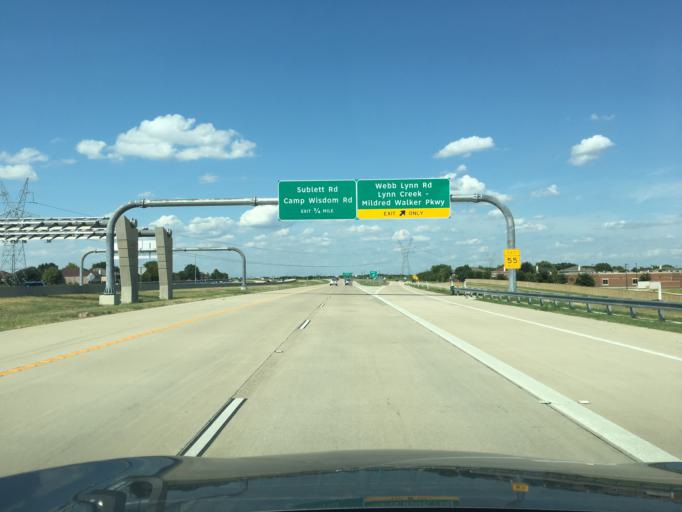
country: US
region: Texas
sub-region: Tarrant County
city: Mansfield
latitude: 32.6274
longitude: -97.0687
